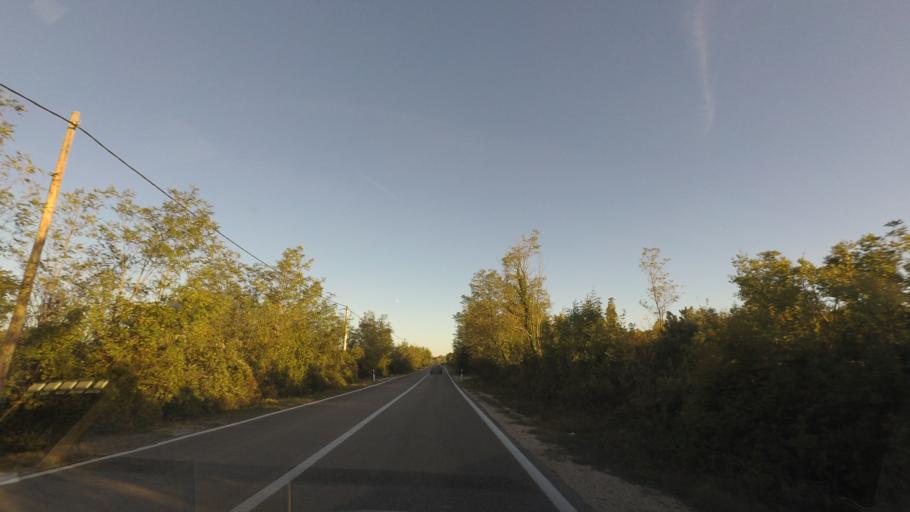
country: HR
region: Zadarska
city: Polaca
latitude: 44.0172
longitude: 15.5388
